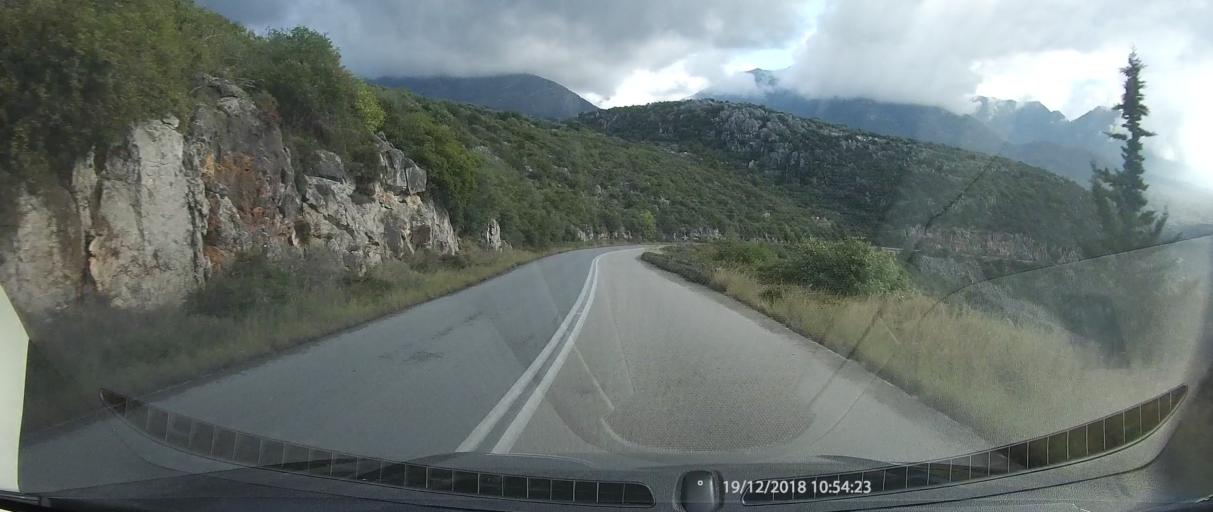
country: GR
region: Peloponnese
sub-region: Nomos Messinias
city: Kardamyli
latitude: 36.9074
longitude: 22.2317
